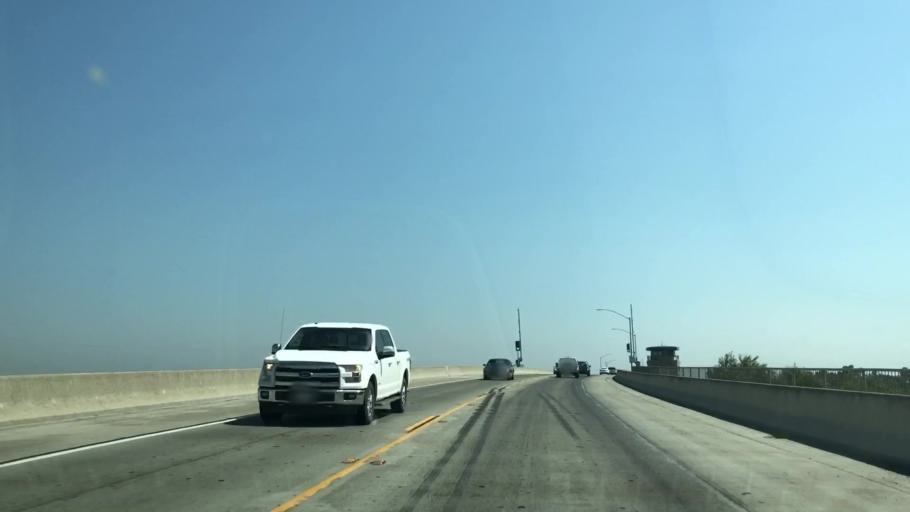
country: US
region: California
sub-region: Sacramento County
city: Walnut Grove
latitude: 38.1146
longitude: -121.5005
